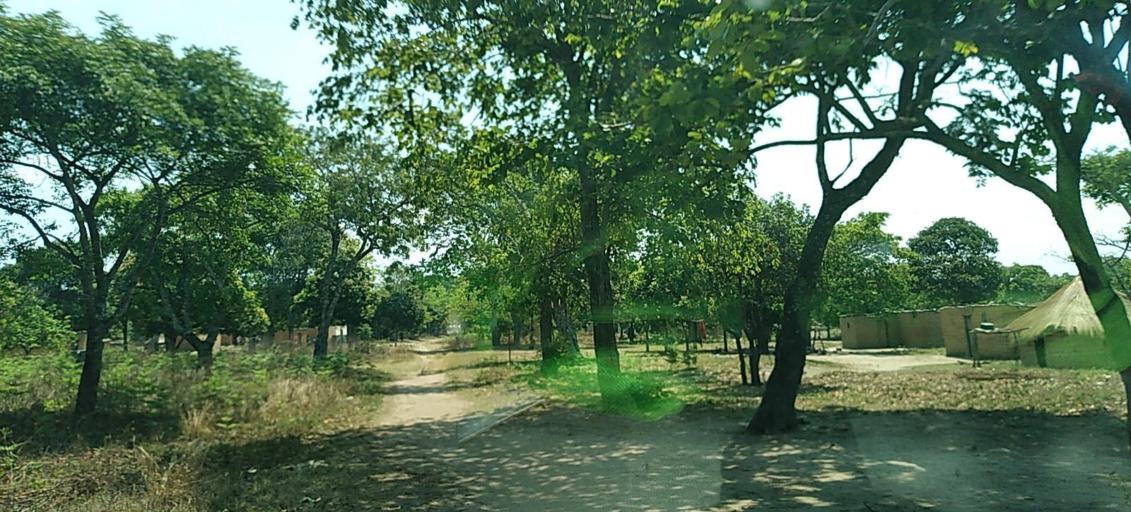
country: CD
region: Katanga
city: Kolwezi
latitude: -11.2810
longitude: 25.1515
